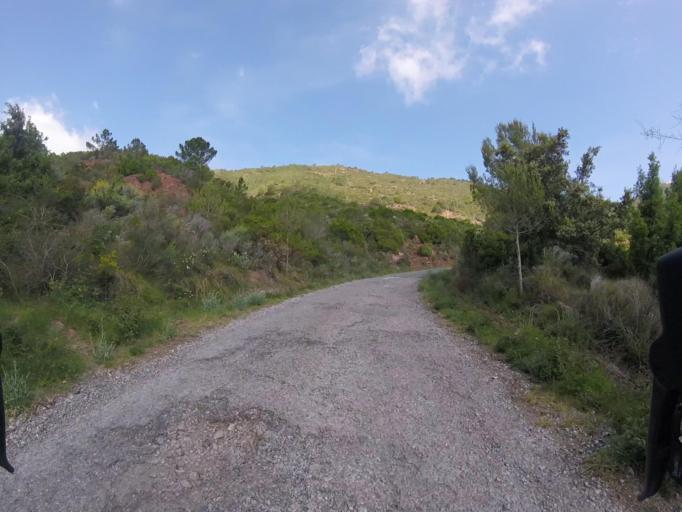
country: ES
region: Valencia
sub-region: Provincia de Castello
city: Benicassim
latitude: 40.0761
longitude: 0.0257
